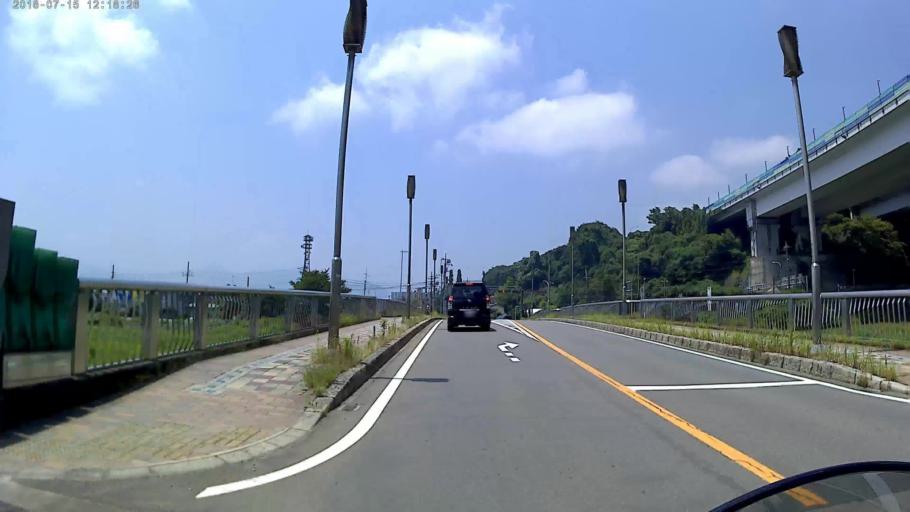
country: JP
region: Kanagawa
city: Hadano
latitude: 35.3475
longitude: 139.1493
